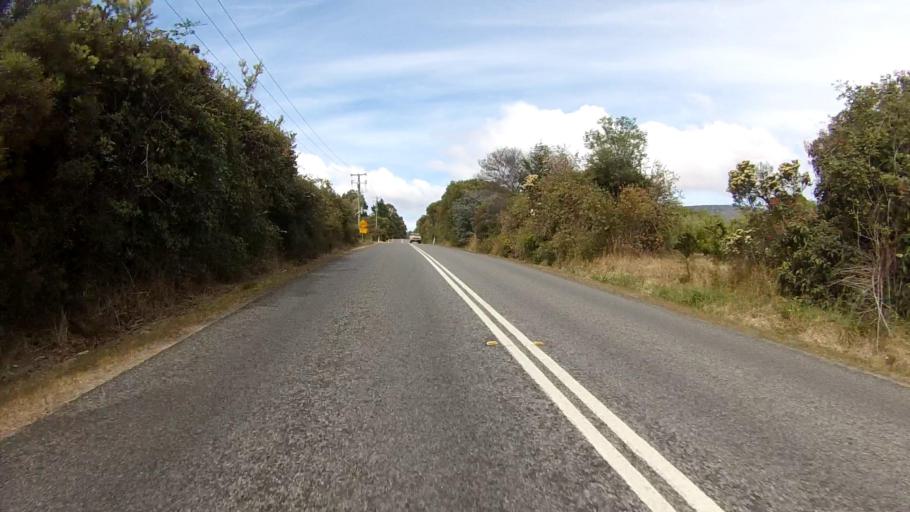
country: AU
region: Tasmania
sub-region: Kingborough
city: Kettering
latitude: -43.1363
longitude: 147.2469
